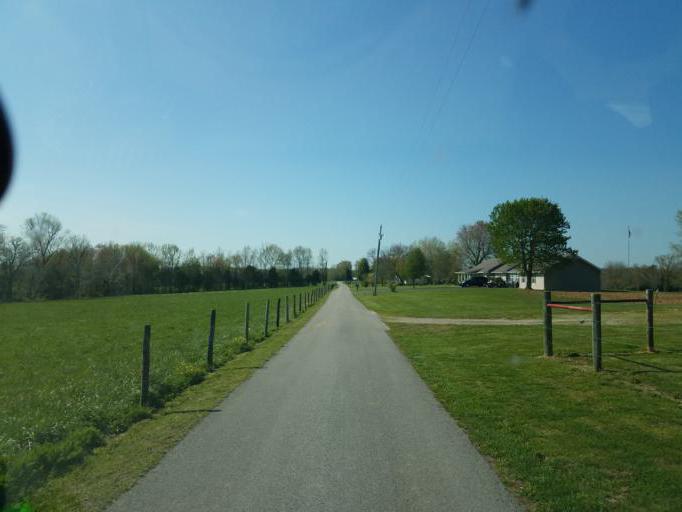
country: US
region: Kentucky
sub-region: Edmonson County
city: Brownsville
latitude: 37.1263
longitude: -86.1488
